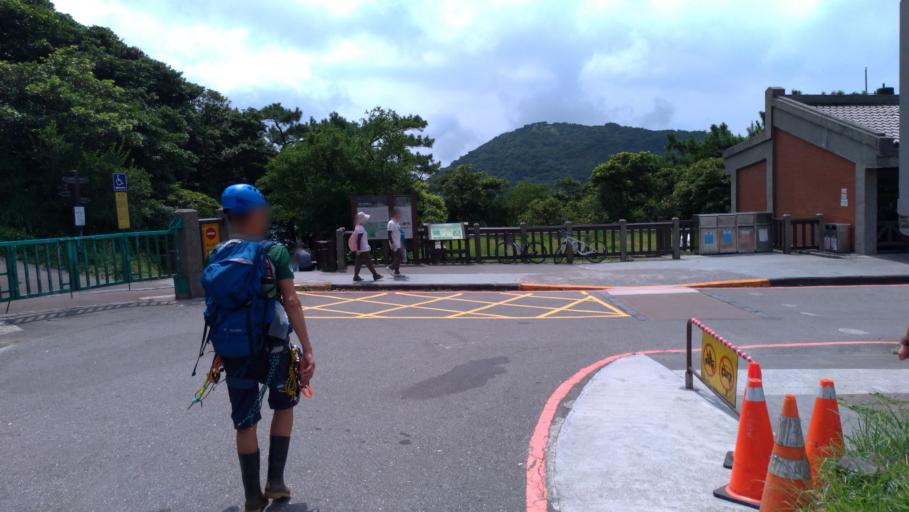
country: TW
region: Taipei
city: Taipei
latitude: 25.1859
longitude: 121.5254
